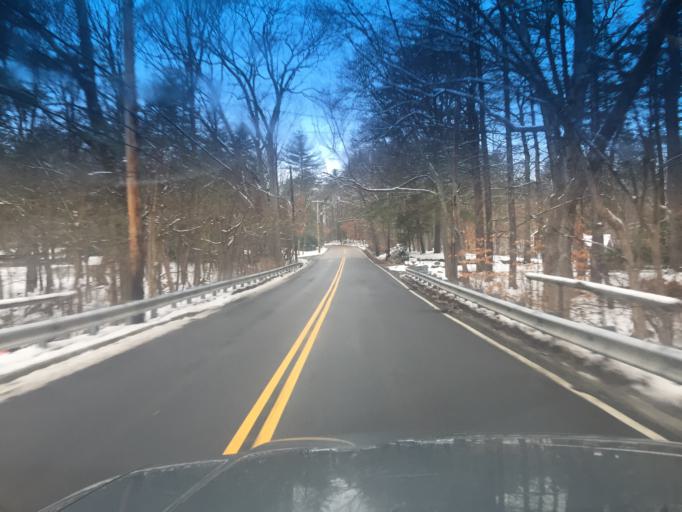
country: US
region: Massachusetts
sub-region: Norfolk County
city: Millis
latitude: 42.1899
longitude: -71.3745
